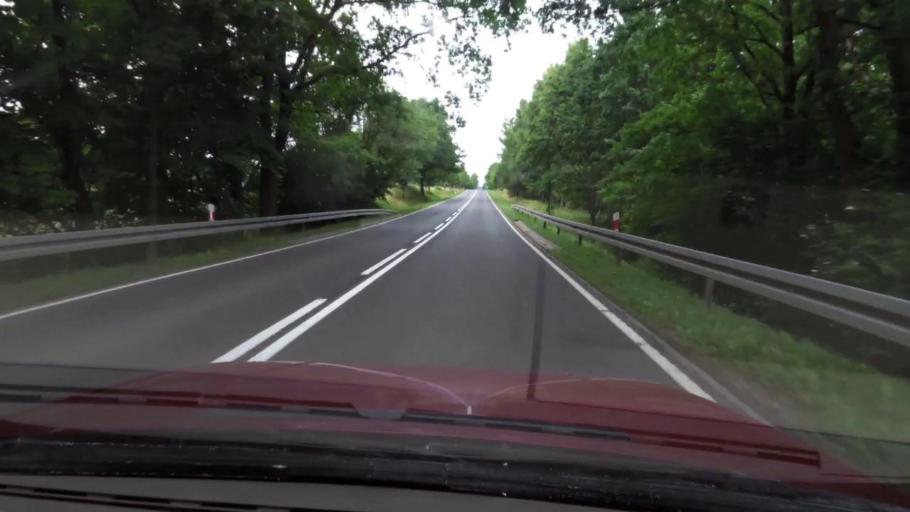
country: PL
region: Pomeranian Voivodeship
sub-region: Powiat bytowski
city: Trzebielino
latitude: 54.2663
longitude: 17.0998
